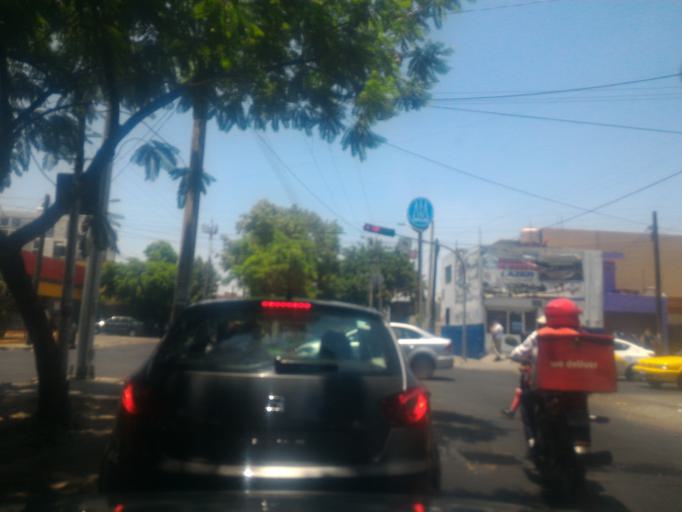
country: MX
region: Jalisco
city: Tlaquepaque
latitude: 20.6626
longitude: -103.2985
